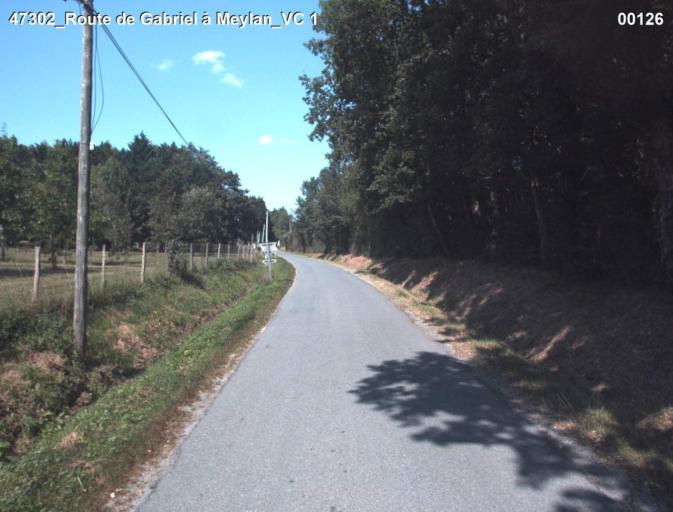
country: FR
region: Aquitaine
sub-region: Departement du Lot-et-Garonne
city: Mezin
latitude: 44.0530
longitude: 0.1423
